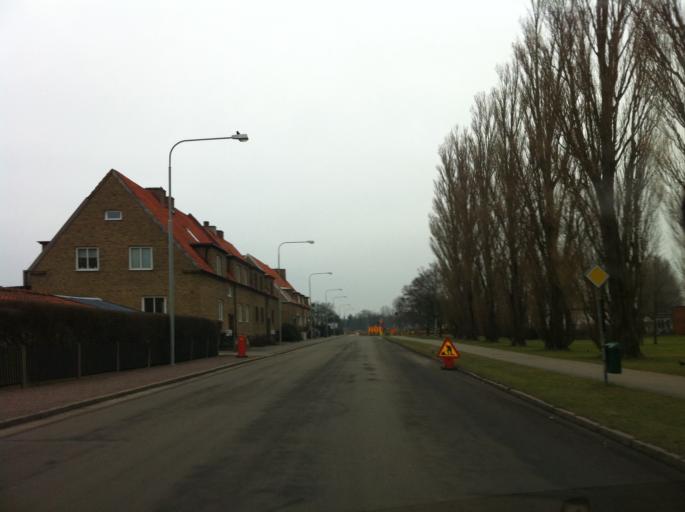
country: SE
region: Skane
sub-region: Landskrona
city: Landskrona
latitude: 55.8978
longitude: 12.8075
